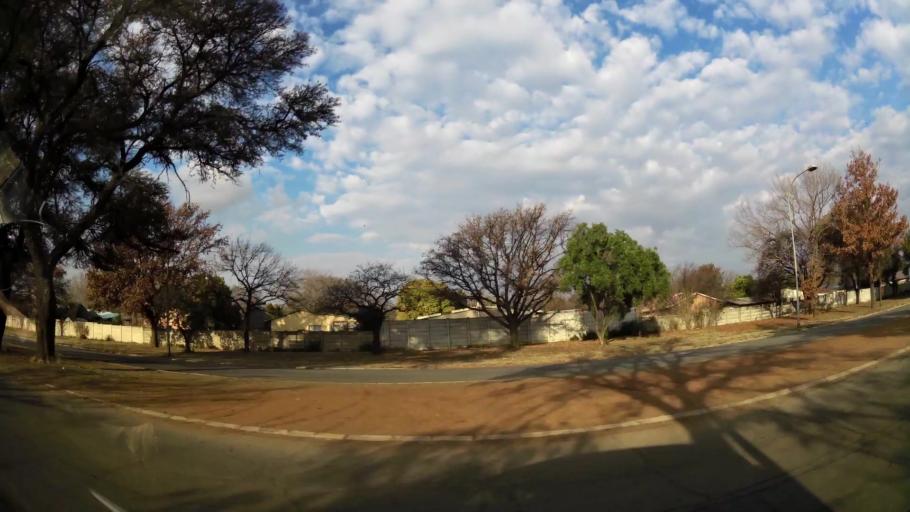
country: ZA
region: Orange Free State
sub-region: Fezile Dabi District Municipality
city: Sasolburg
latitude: -26.8187
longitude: 27.8089
